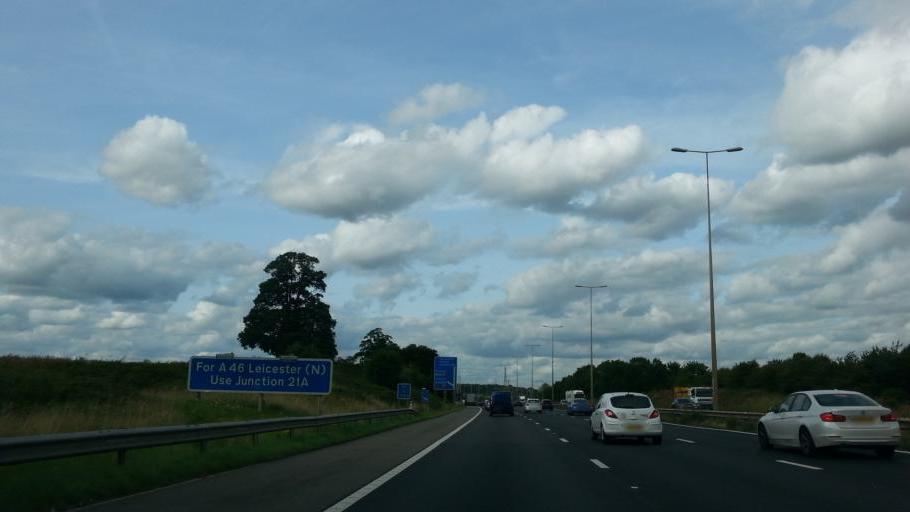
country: GB
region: England
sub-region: Leicestershire
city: Enderby
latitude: 52.5932
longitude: -1.1953
